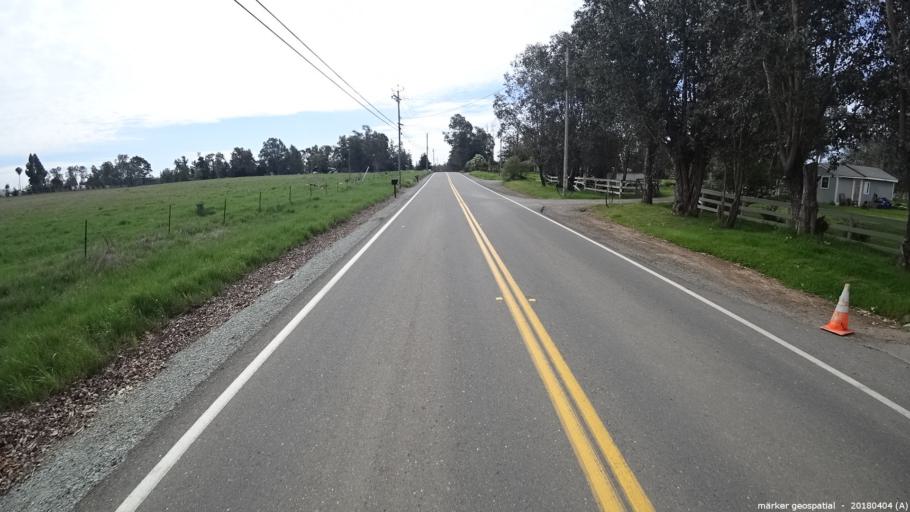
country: US
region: California
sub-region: Sacramento County
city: Clay
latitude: 38.3128
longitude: -121.1712
